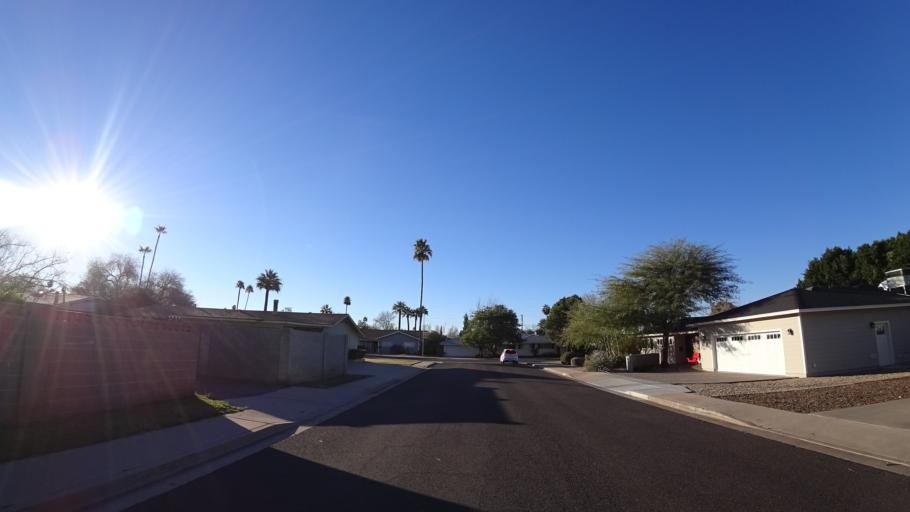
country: US
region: Arizona
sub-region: Maricopa County
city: Paradise Valley
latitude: 33.5001
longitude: -112.0103
